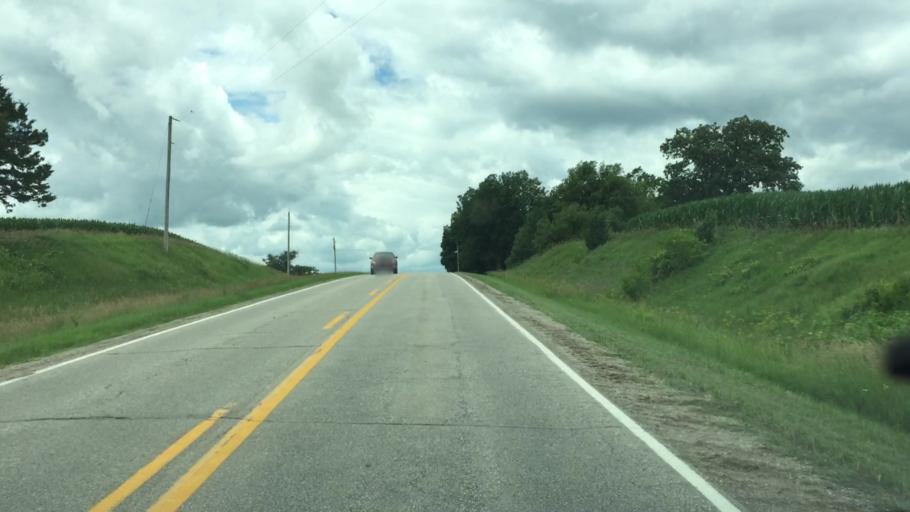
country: US
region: Iowa
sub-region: Jasper County
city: Monroe
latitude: 41.5735
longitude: -93.0472
